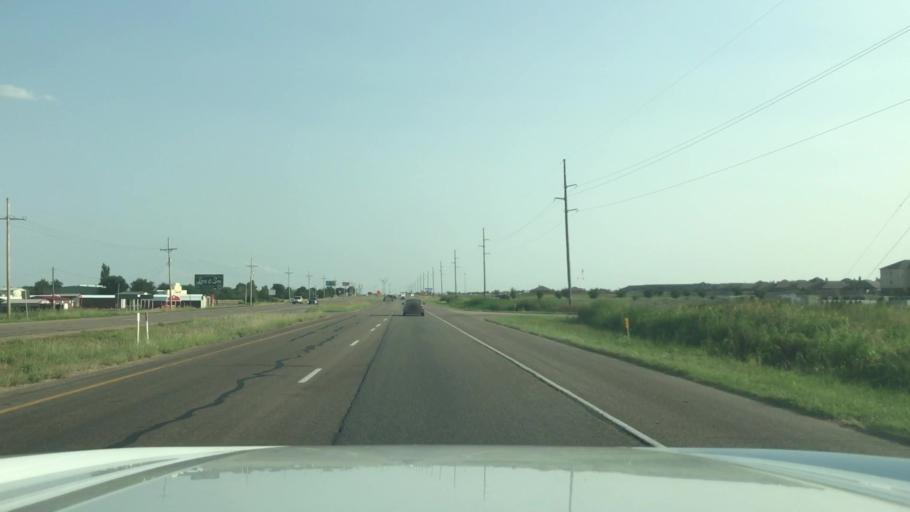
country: US
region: Texas
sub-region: Potter County
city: Amarillo
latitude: 35.1326
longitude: -101.9382
